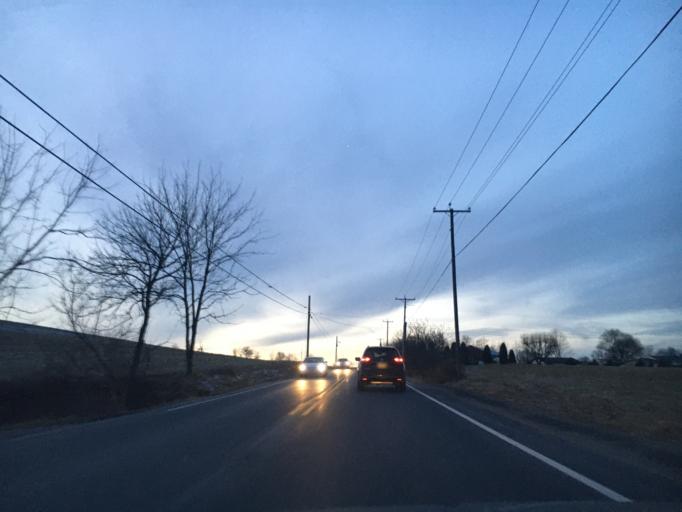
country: US
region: Pennsylvania
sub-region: Northampton County
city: Youngsville
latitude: 40.7527
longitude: -75.4892
